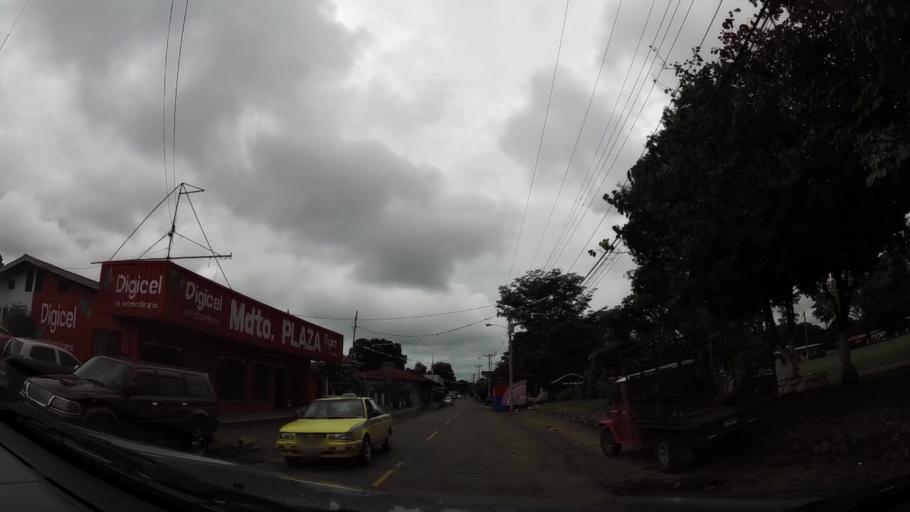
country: PA
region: Chiriqui
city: Dolega District
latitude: 8.5636
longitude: -82.4147
